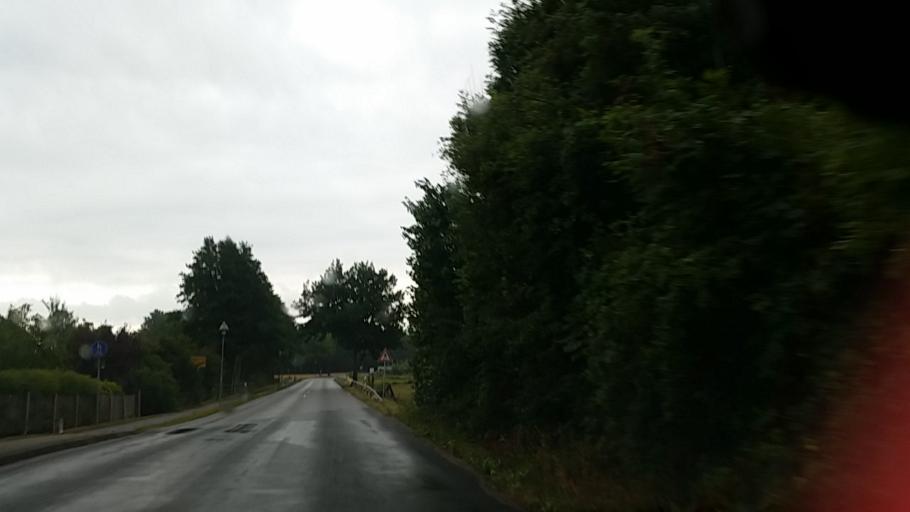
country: DE
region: Lower Saxony
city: Bokensdorf
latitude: 52.4956
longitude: 10.7134
